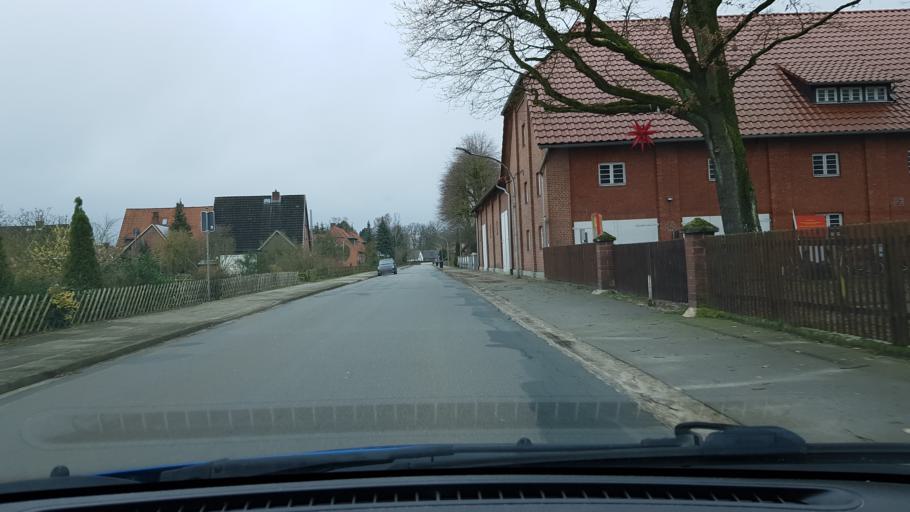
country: DE
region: Lower Saxony
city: Wrestedt
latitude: 52.9070
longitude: 10.5722
